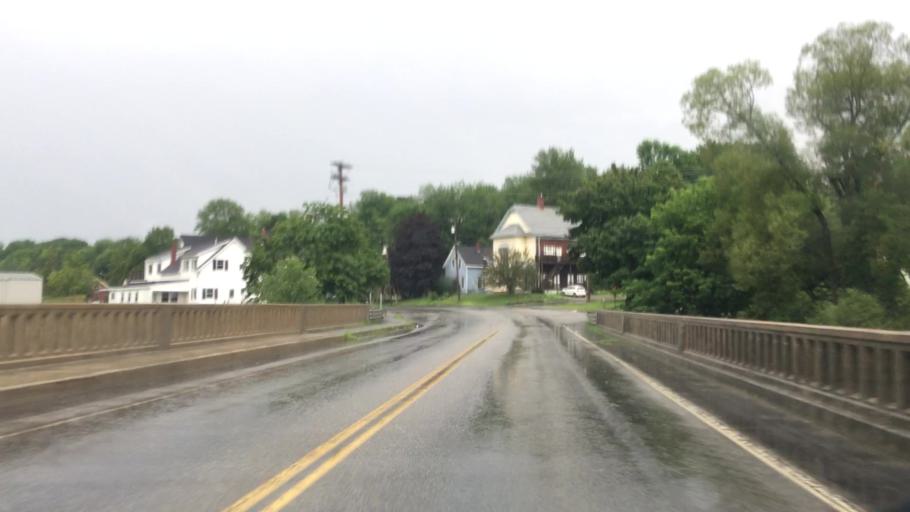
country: US
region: Maine
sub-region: Kennebec County
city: Gardiner
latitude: 44.2200
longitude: -69.7901
